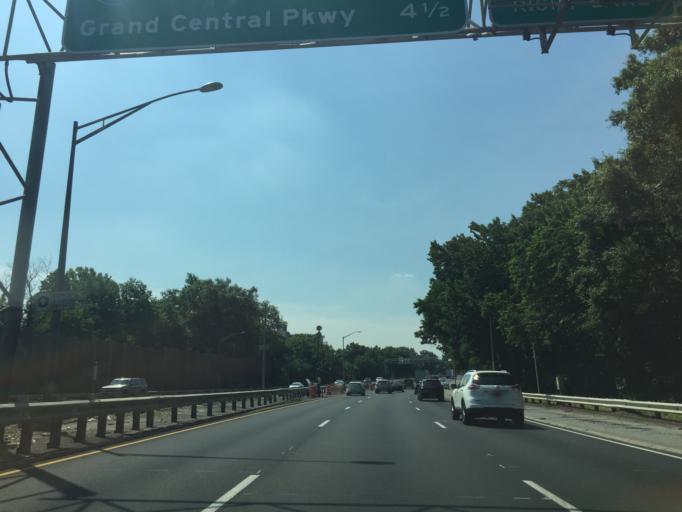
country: US
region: New York
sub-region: Nassau County
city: East Atlantic Beach
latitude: 40.7835
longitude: -73.7858
